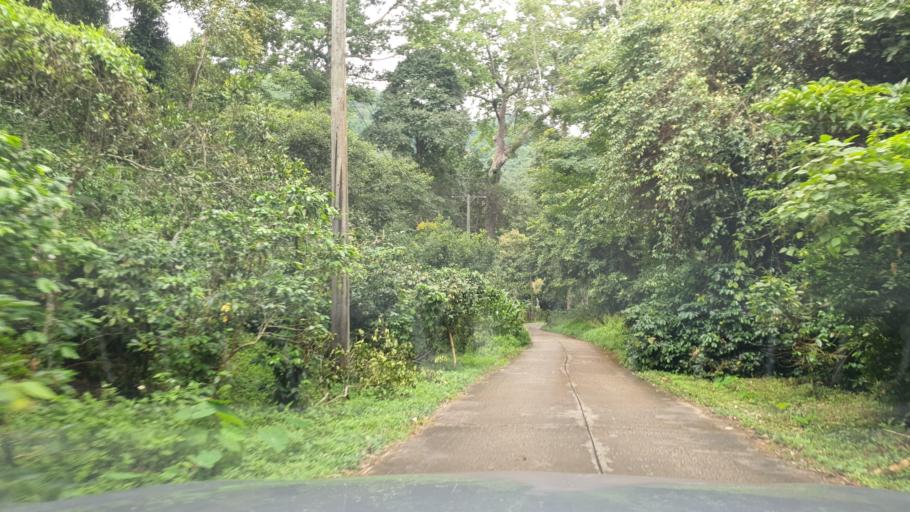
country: TH
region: Chiang Mai
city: Mae Taeng
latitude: 19.2396
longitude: 98.9284
